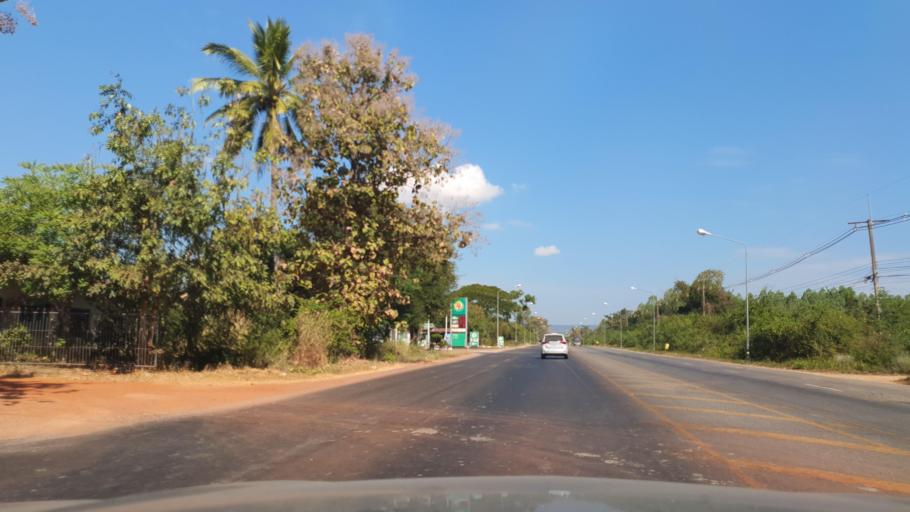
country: TH
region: Kalasin
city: Somdet
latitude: 16.7293
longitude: 103.7630
